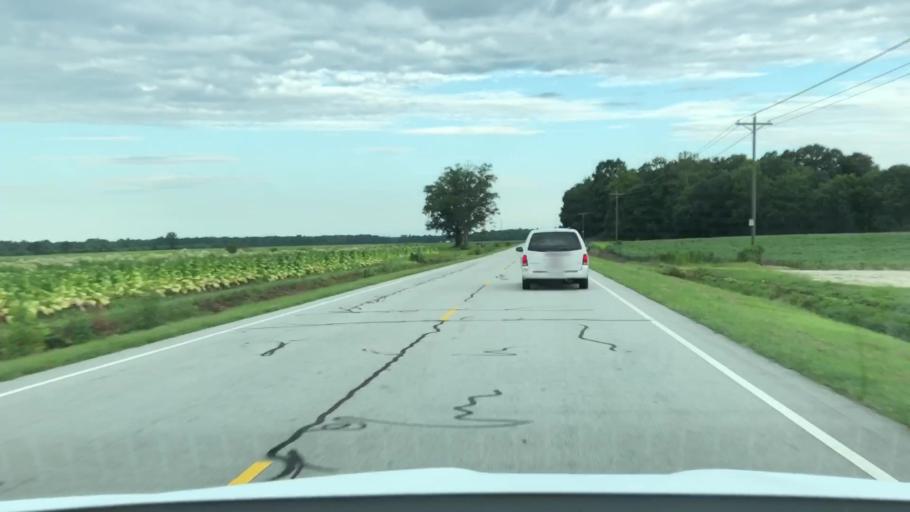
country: US
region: North Carolina
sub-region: Jones County
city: Trenton
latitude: 35.0787
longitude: -77.4258
